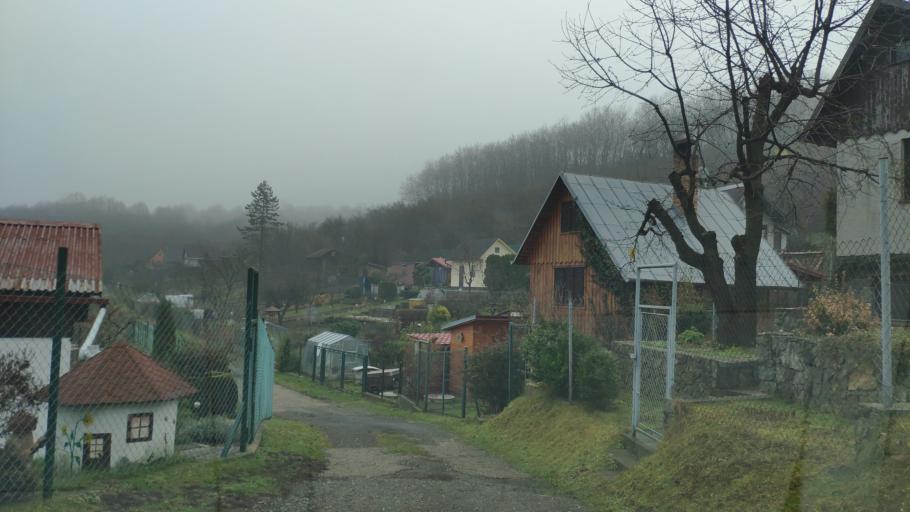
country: SK
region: Kosicky
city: Kosice
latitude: 48.7111
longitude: 21.3582
